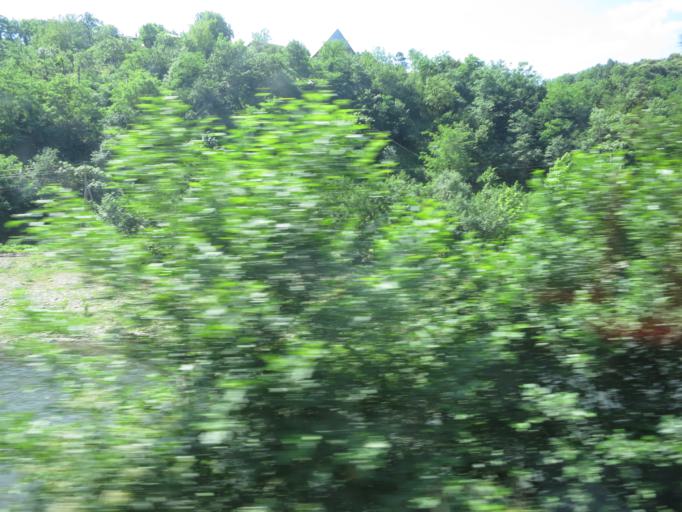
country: GE
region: Imereti
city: Kharagauli
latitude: 42.0794
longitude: 43.1603
